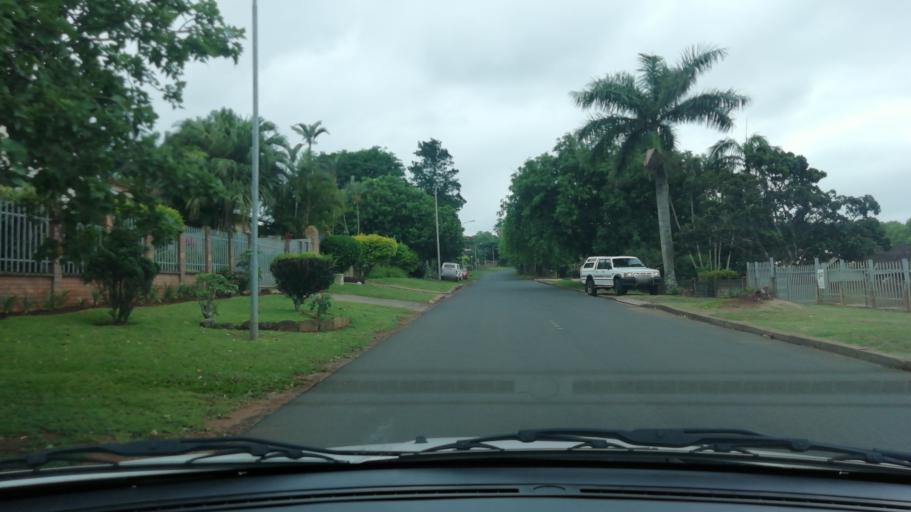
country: ZA
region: KwaZulu-Natal
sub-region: uThungulu District Municipality
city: Empangeni
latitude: -28.7672
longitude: 31.8921
